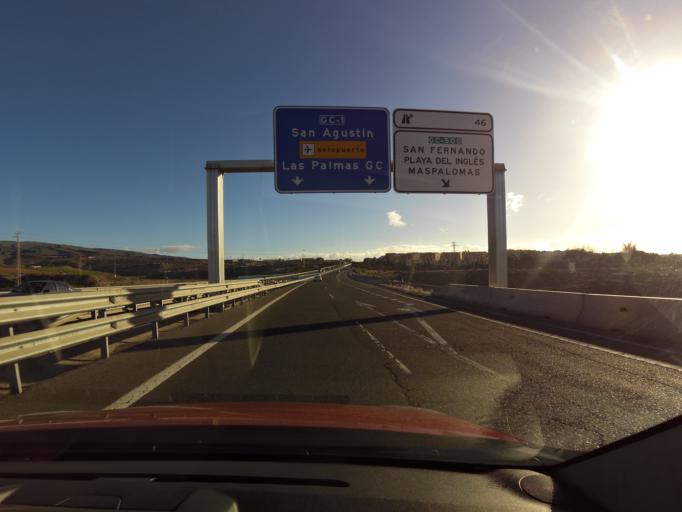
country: ES
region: Canary Islands
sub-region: Provincia de Las Palmas
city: Maspalomas
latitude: 27.7705
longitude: -15.5946
